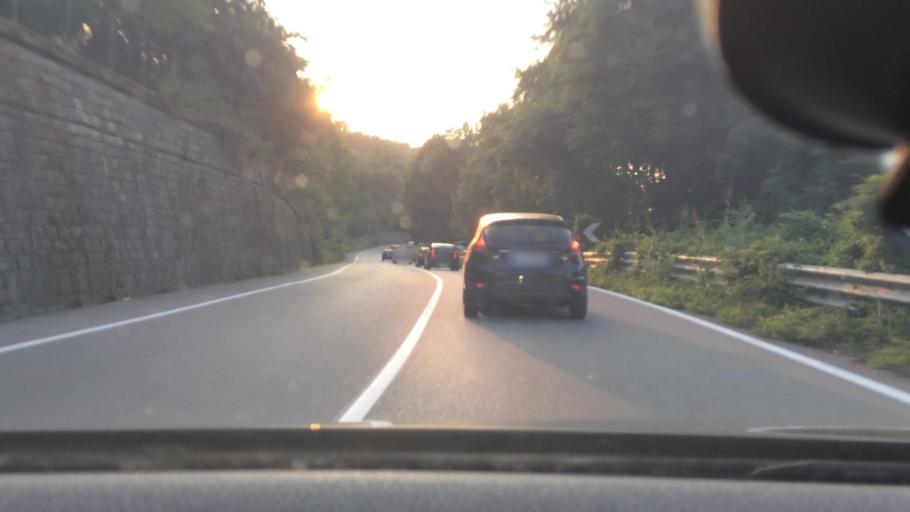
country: IT
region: Lombardy
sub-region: Provincia di Lecco
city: Perego
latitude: 45.7424
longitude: 9.3521
